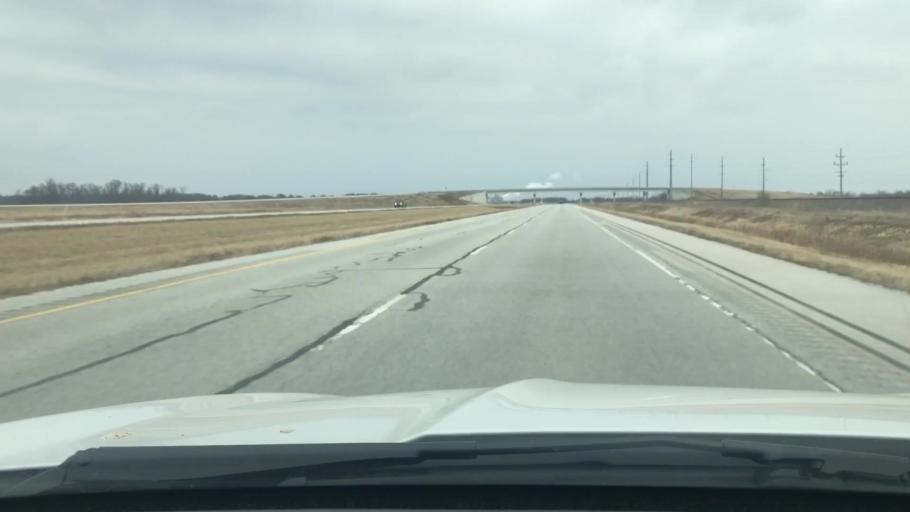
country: US
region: Indiana
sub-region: Cass County
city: Georgetown
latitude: 40.6899
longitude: -86.4828
